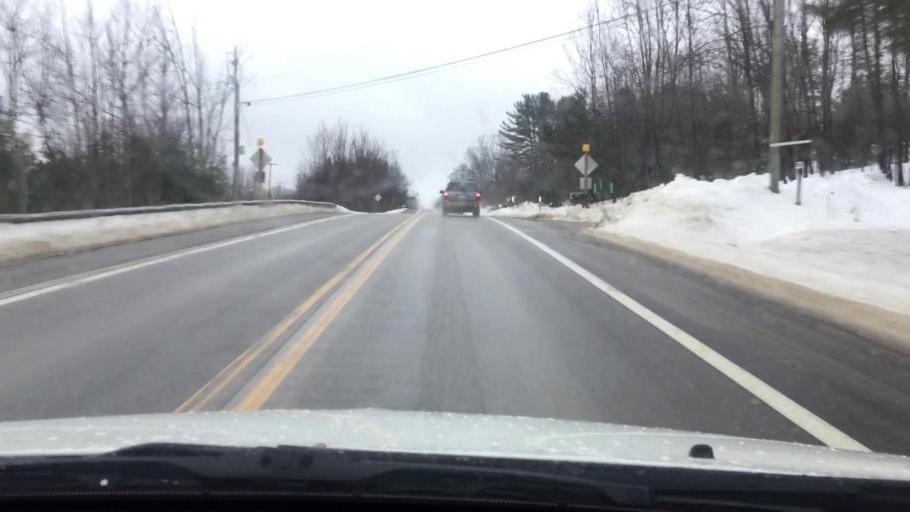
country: US
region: Michigan
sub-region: Charlevoix County
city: East Jordan
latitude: 45.2457
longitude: -85.1809
